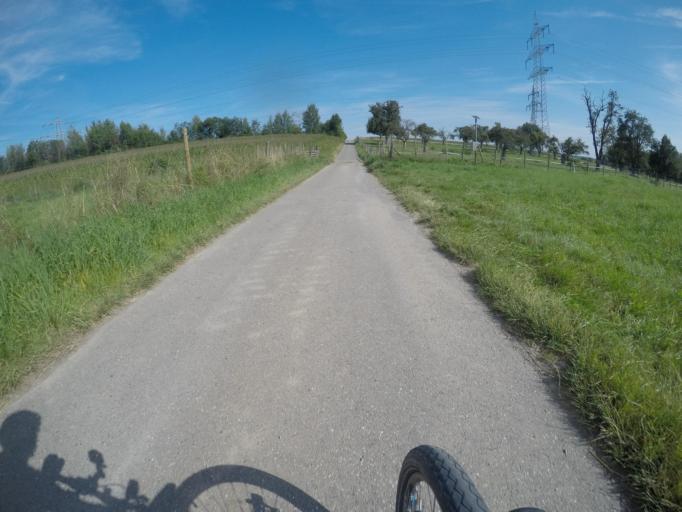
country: DE
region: Baden-Wuerttemberg
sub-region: Karlsruhe Region
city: Wiernsheim
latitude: 48.8994
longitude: 8.8544
